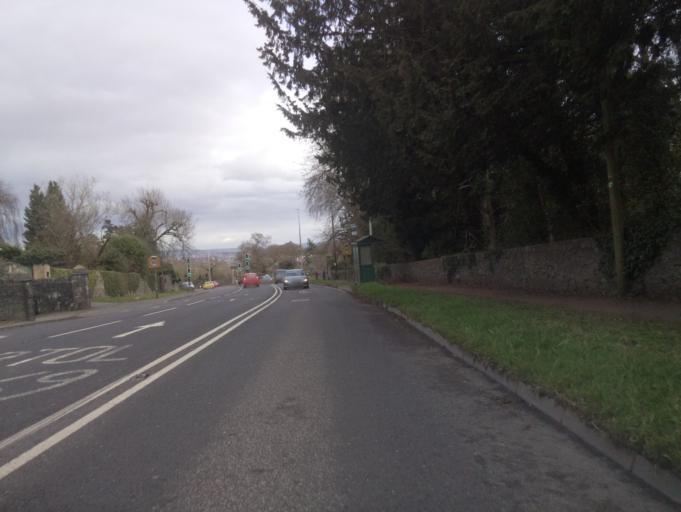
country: GB
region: England
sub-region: North Somerset
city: Long Ashton
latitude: 51.4521
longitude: -2.6384
